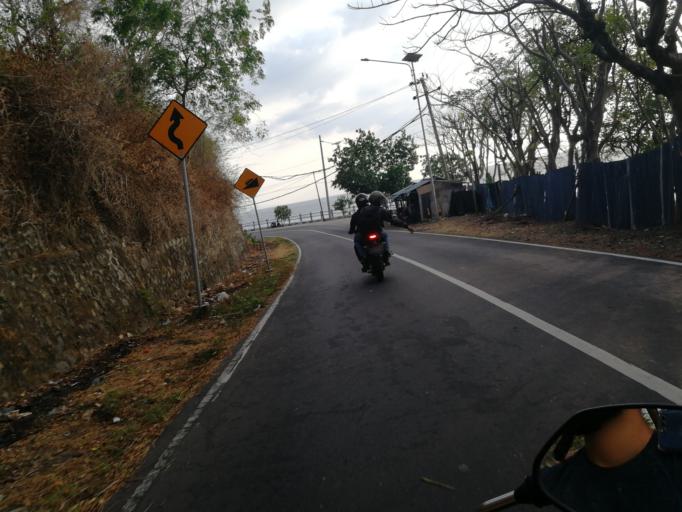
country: ID
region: West Nusa Tenggara
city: Karangsubagan
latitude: -8.4618
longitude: 116.0365
